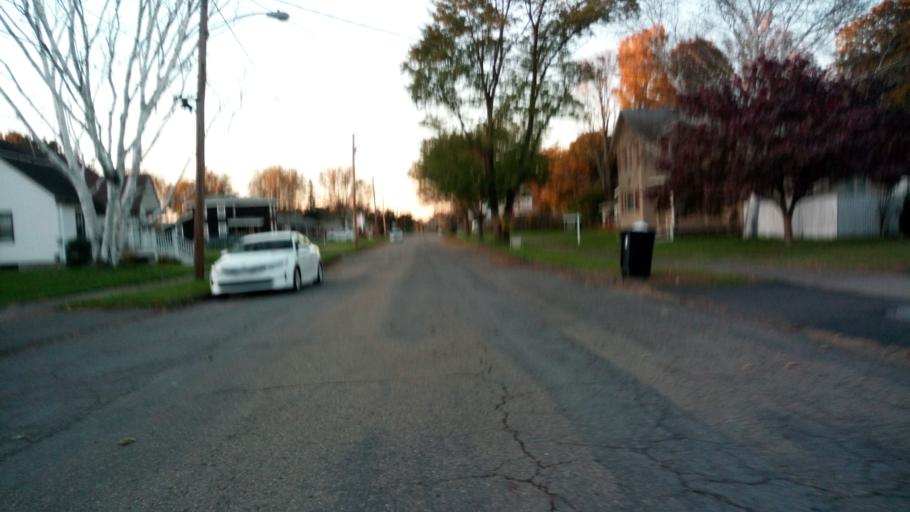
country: US
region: New York
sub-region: Chemung County
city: Elmira
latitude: 42.0810
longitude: -76.8110
